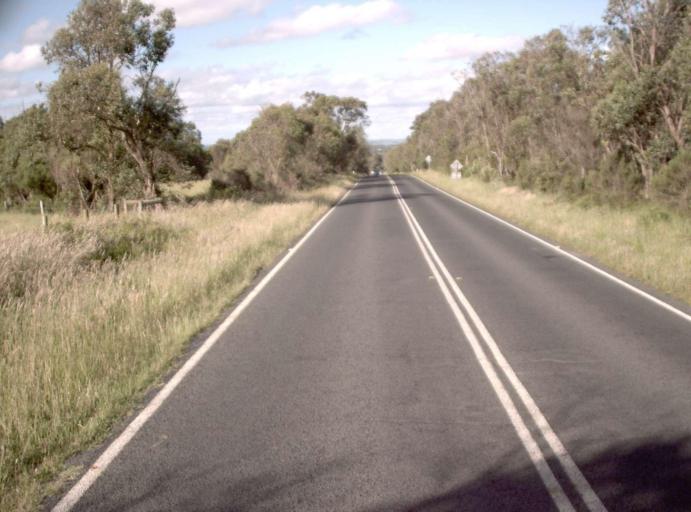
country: AU
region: Victoria
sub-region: Bass Coast
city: North Wonthaggi
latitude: -38.5517
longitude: 145.8458
